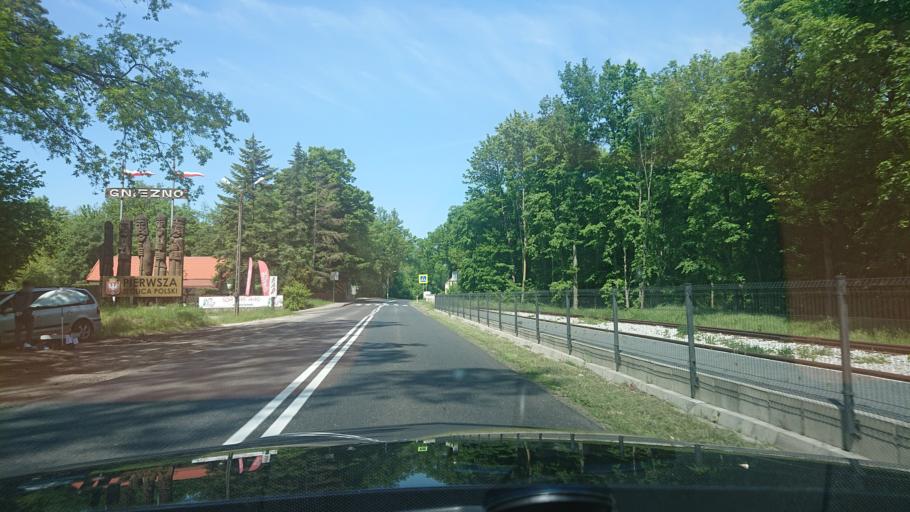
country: PL
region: Greater Poland Voivodeship
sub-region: Powiat gnieznienski
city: Gniezno
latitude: 52.5048
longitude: 17.6255
